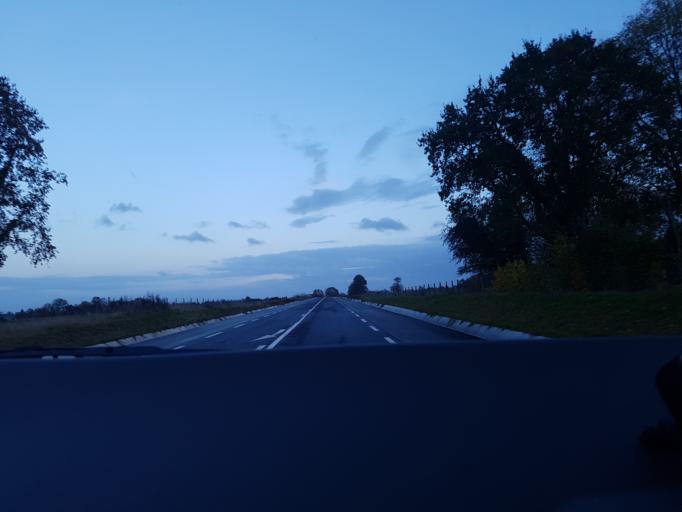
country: FR
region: Haute-Normandie
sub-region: Departement de l'Eure
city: Beuzeville
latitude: 49.3293
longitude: 0.3173
